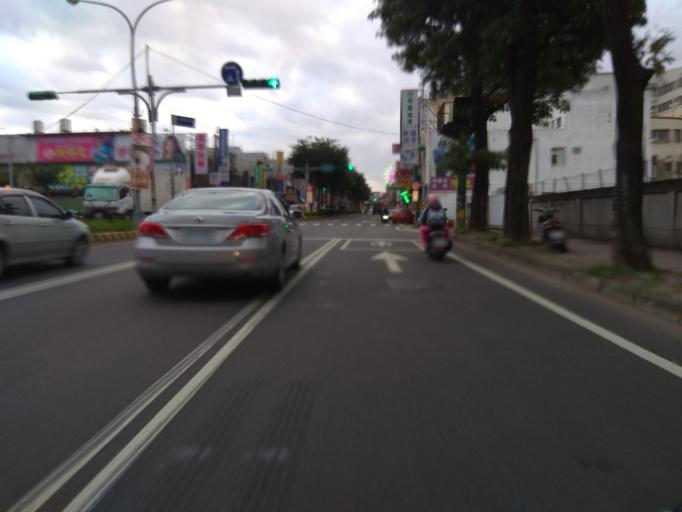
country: TW
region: Taiwan
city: Daxi
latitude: 24.9028
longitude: 121.2117
